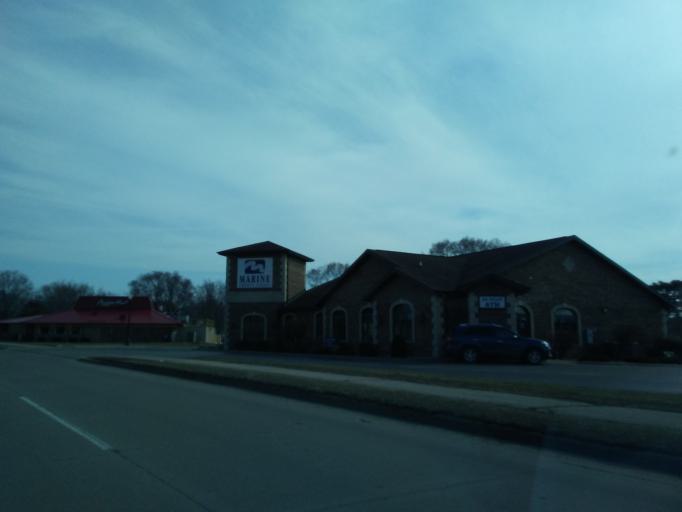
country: US
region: Wisconsin
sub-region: Crawford County
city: Prairie du Chien
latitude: 43.0347
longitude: -91.1375
